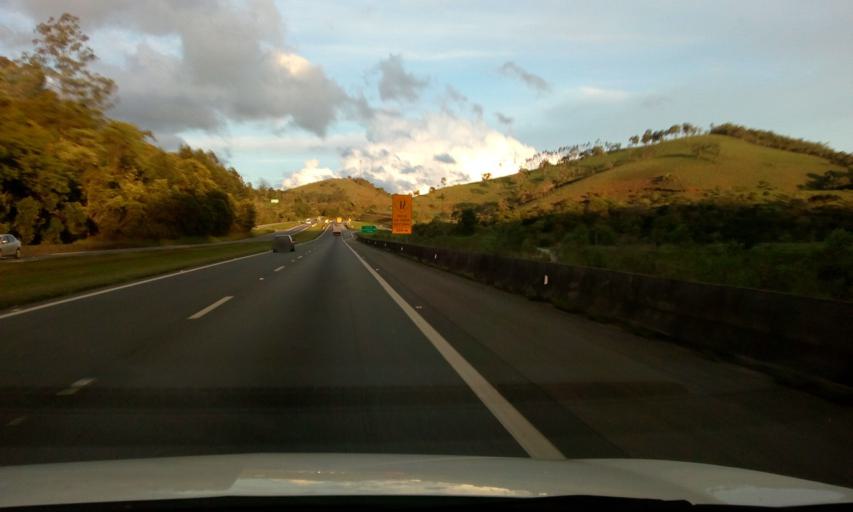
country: BR
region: Sao Paulo
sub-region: Piracaia
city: Piracaia
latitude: -23.1727
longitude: -46.2698
